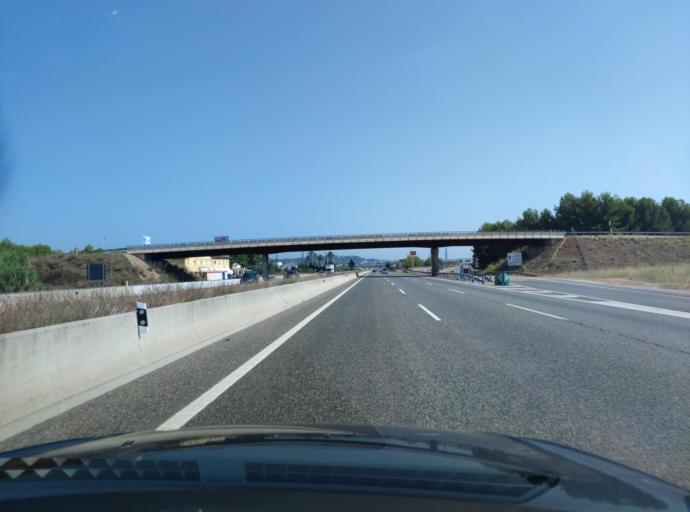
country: ES
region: Valencia
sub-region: Provincia de Valencia
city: Beneixida
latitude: 39.0575
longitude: -0.5442
